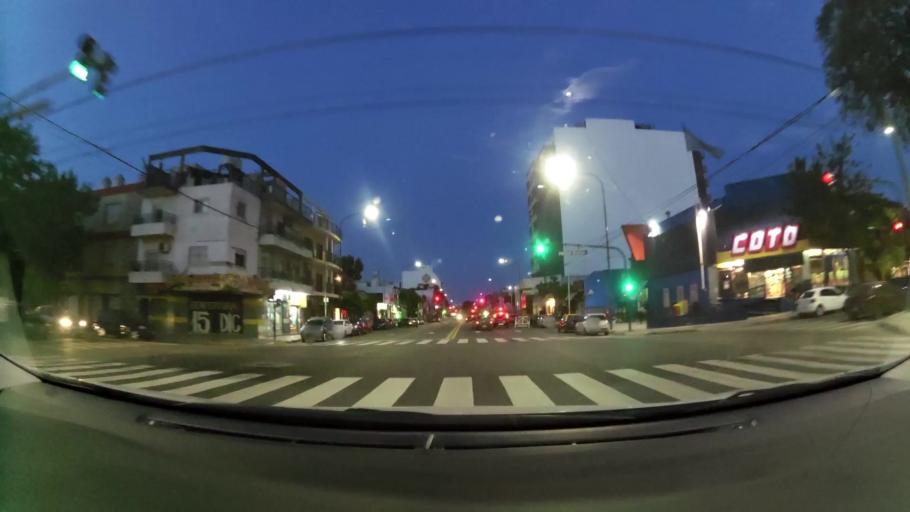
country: AR
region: Buenos Aires F.D.
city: Villa Lugano
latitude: -34.6875
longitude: -58.4754
